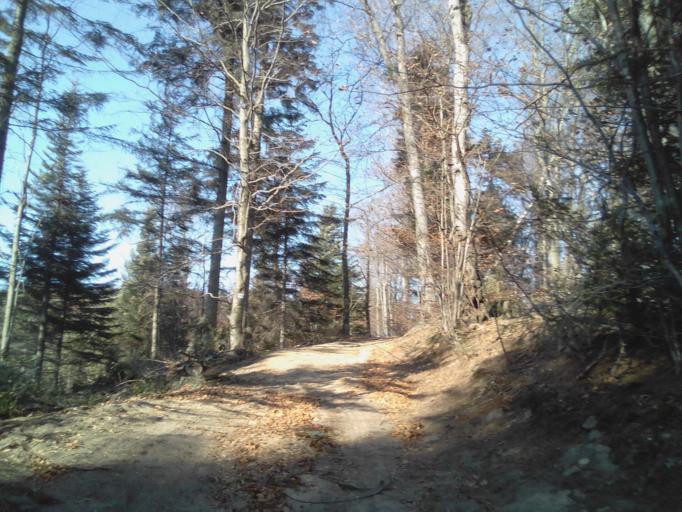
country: PL
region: Subcarpathian Voivodeship
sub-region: Powiat strzyzowski
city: Wysoka Strzyzowska
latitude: 49.8126
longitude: 21.7156
